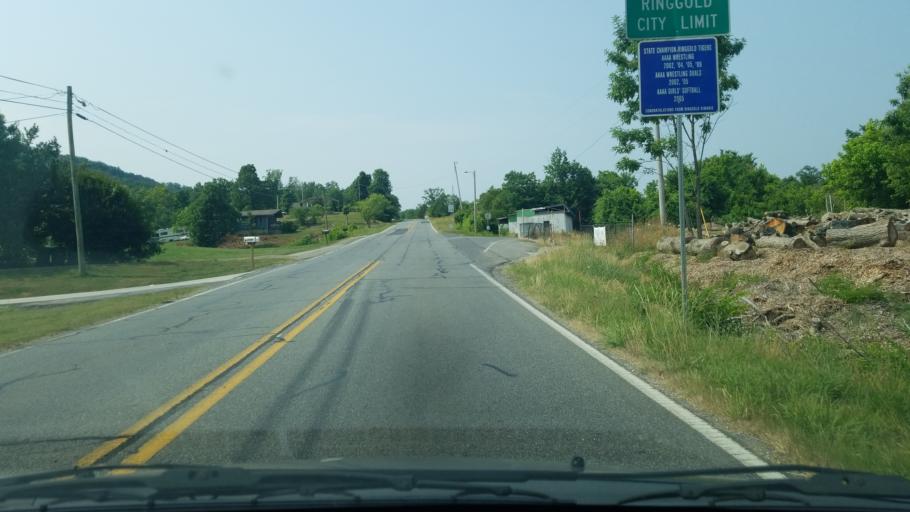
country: US
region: Georgia
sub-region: Catoosa County
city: Ringgold
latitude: 34.9272
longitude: -85.1038
